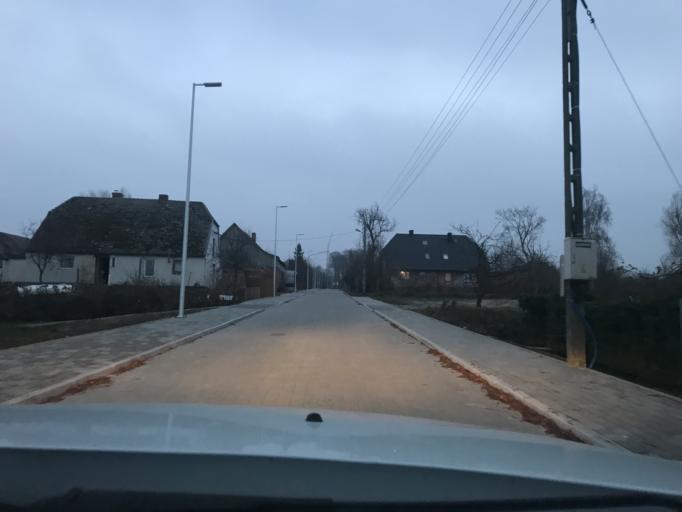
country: PL
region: West Pomeranian Voivodeship
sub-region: Powiat slawienski
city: Darlowo
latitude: 54.4808
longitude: 16.5084
